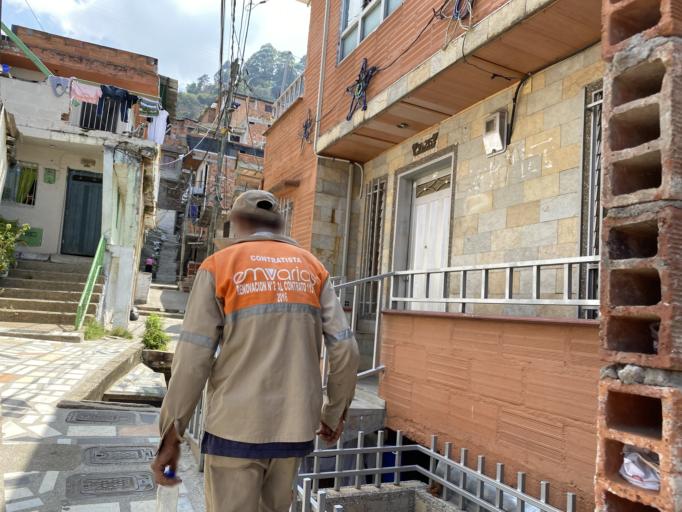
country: CO
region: Antioquia
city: Medellin
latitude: 6.2674
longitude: -75.5436
